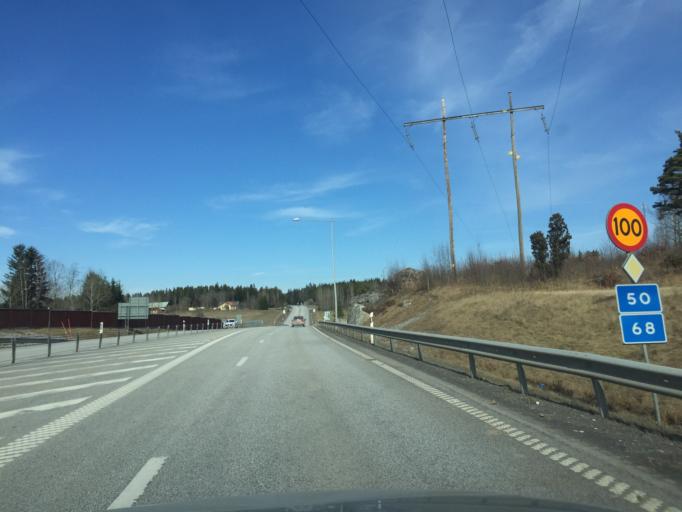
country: SE
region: OErebro
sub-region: Orebro Kommun
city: Hovsta
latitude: 59.3713
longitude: 15.2197
